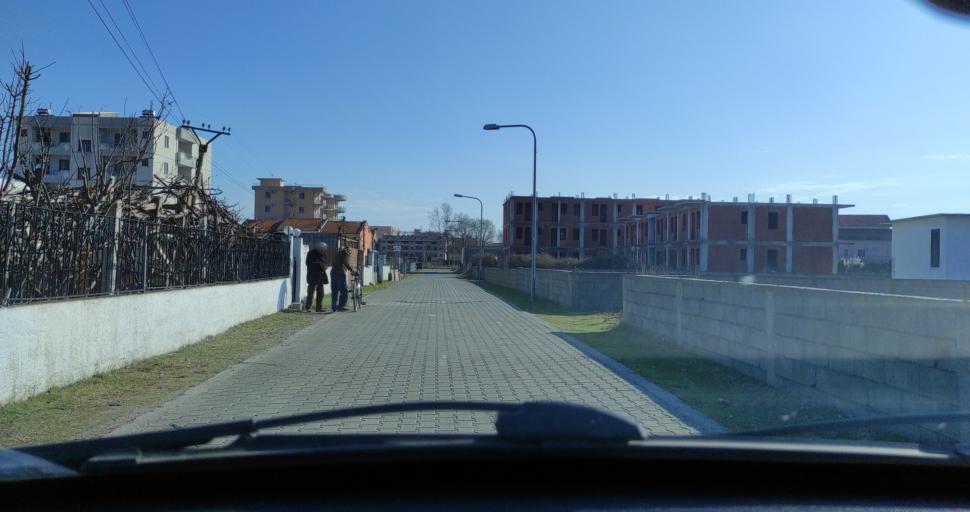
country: AL
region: Shkoder
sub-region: Rrethi i Shkodres
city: Velipoje
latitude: 41.8678
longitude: 19.4212
